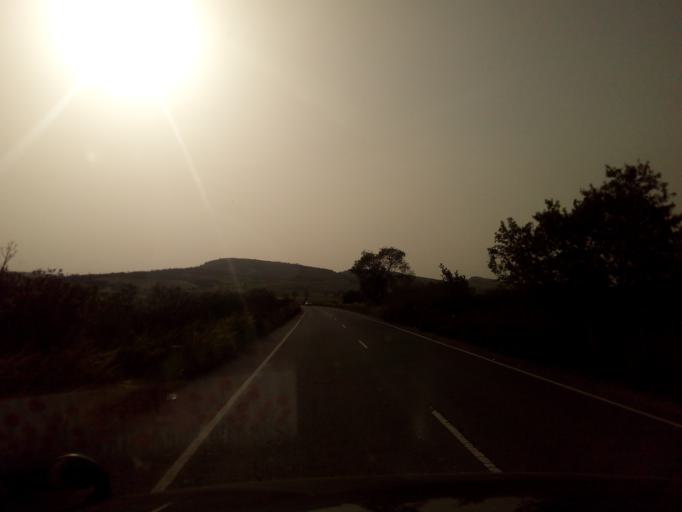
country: CY
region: Lefkosia
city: Lympia
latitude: 35.0015
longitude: 33.4950
